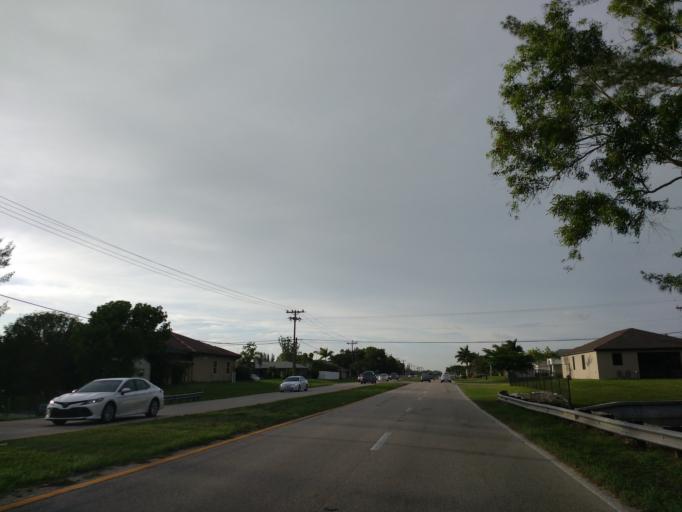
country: US
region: Florida
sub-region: Lee County
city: Cape Coral
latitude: 26.5996
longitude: -82.0070
